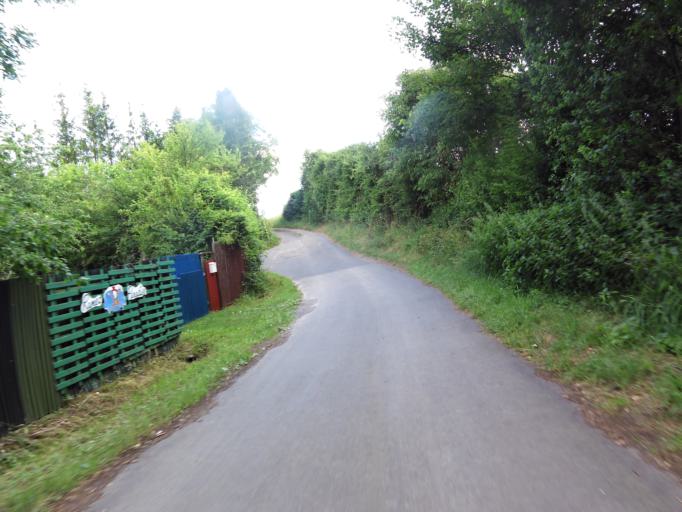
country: DE
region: Bavaria
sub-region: Regierungsbezirk Unterfranken
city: Wuerzburg
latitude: 49.8107
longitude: 9.9294
